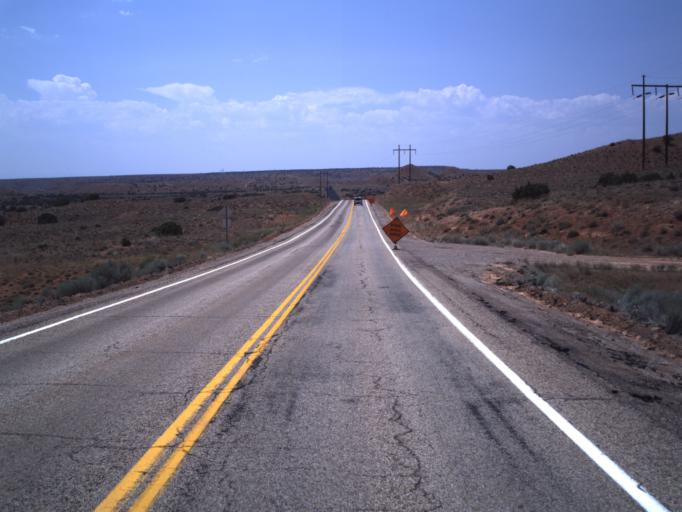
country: US
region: Utah
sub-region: Uintah County
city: Maeser
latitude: 40.4208
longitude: -109.6693
